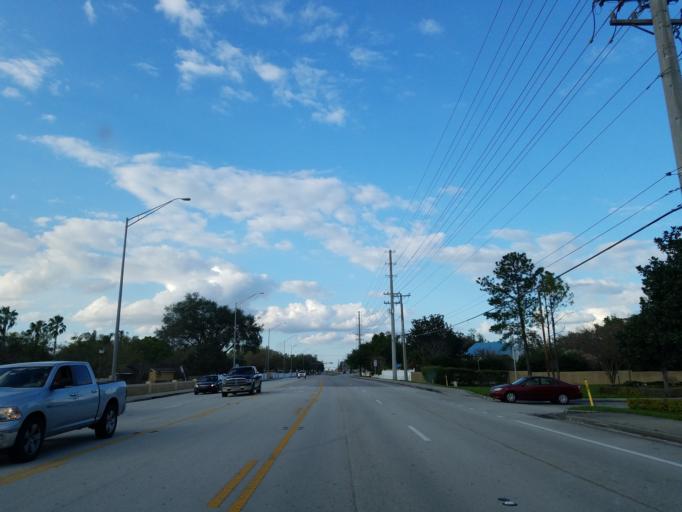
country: US
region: Florida
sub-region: Polk County
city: Lakeland Highlands
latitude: 27.9540
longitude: -81.9236
